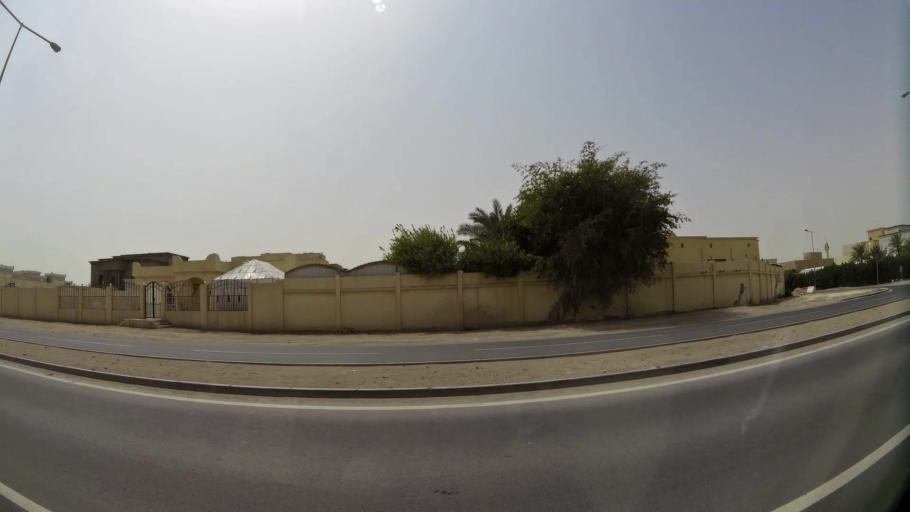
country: QA
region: Baladiyat ar Rayyan
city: Ar Rayyan
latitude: 25.2389
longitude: 51.3812
